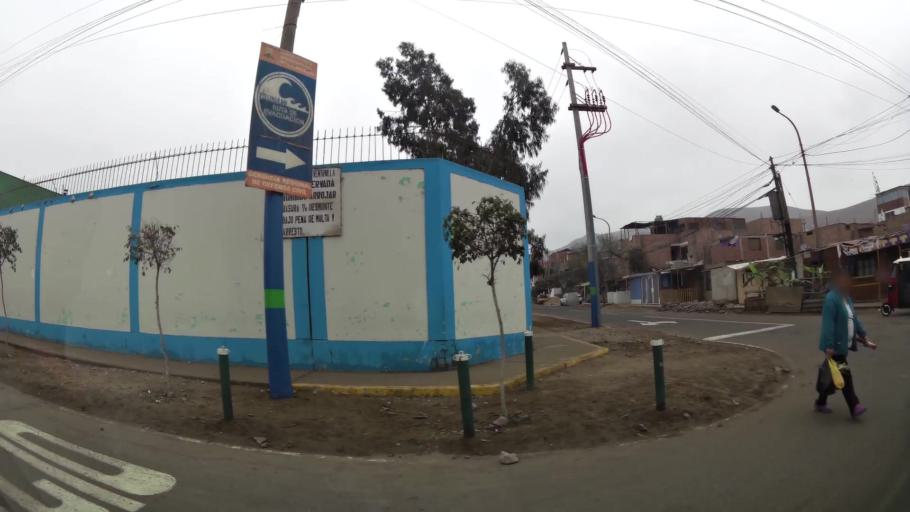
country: PE
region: Lima
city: Ventanilla
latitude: -11.8821
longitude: -77.1311
